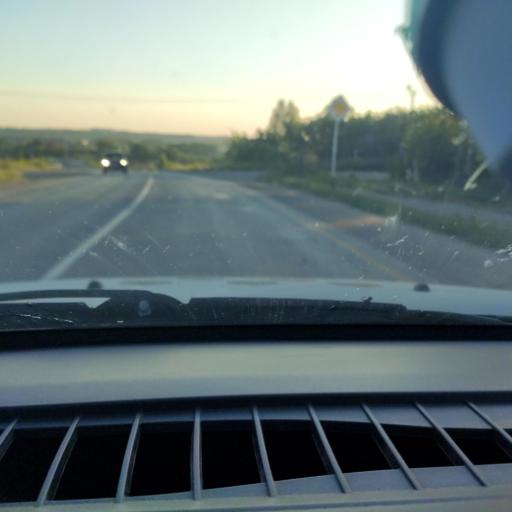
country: RU
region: Perm
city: Kungur
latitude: 57.4448
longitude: 56.9578
